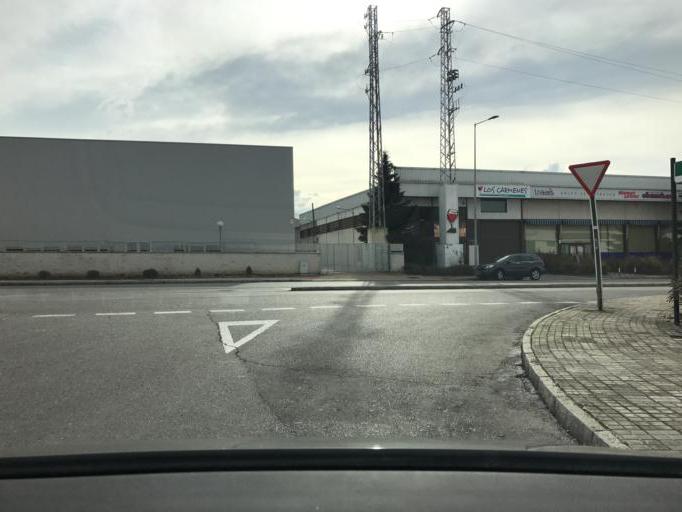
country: ES
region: Andalusia
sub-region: Provincia de Granada
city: Peligros
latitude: 37.2242
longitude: -3.6255
